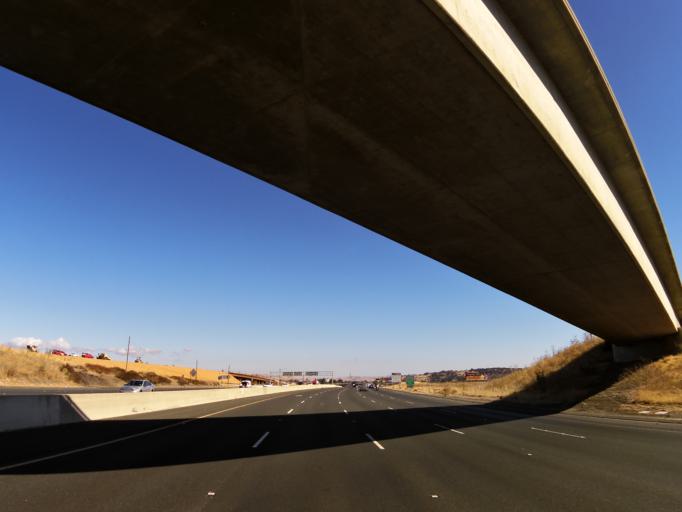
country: US
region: California
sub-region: Solano County
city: Green Valley
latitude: 38.2081
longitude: -122.1500
